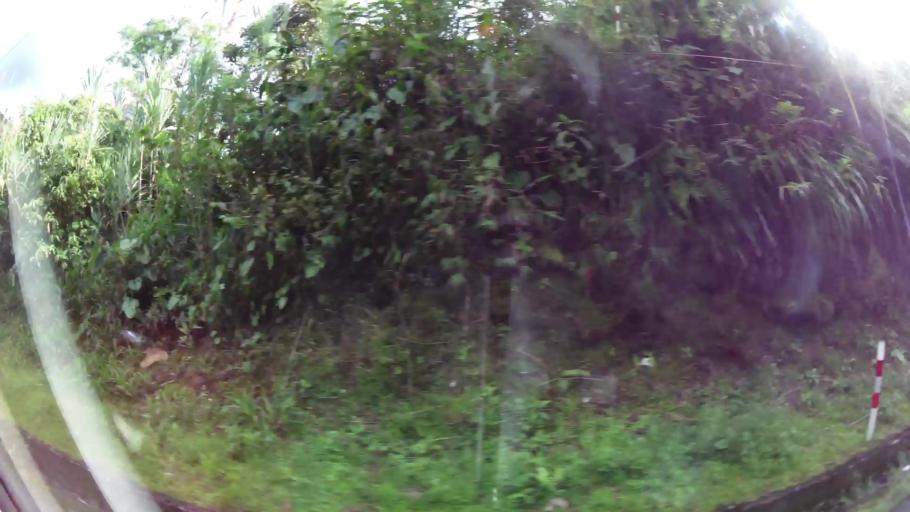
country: EC
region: Pastaza
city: Puyo
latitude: -1.4162
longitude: -78.1786
